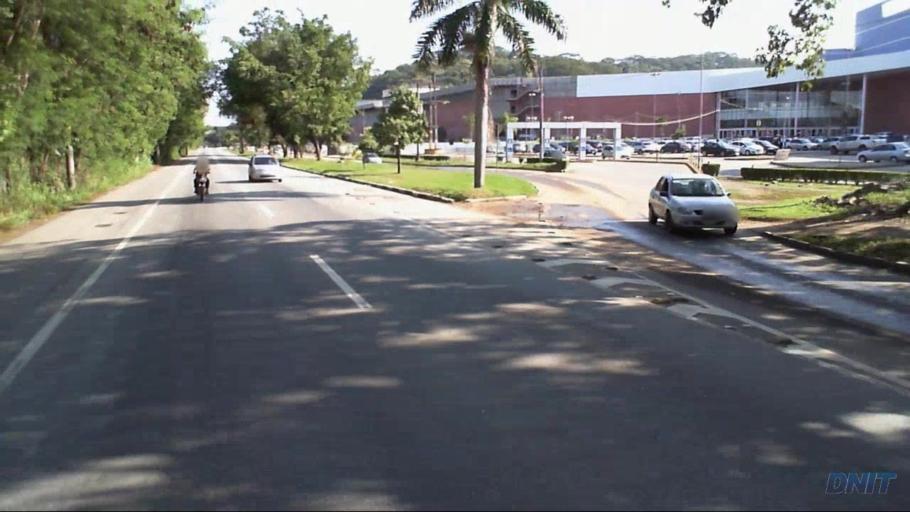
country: BR
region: Minas Gerais
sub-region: Ipatinga
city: Ipatinga
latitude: -19.4954
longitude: -42.5642
